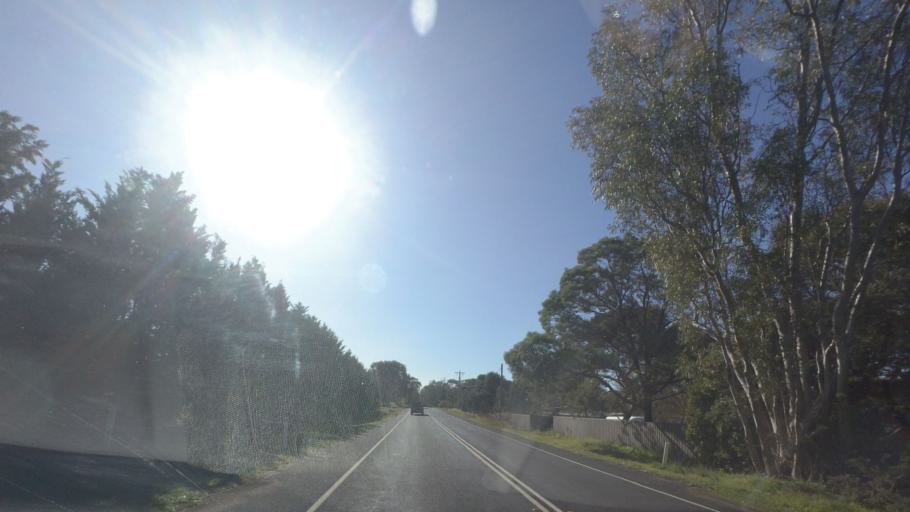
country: AU
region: Victoria
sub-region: Greater Bendigo
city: Kennington
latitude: -36.8806
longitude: 144.3133
